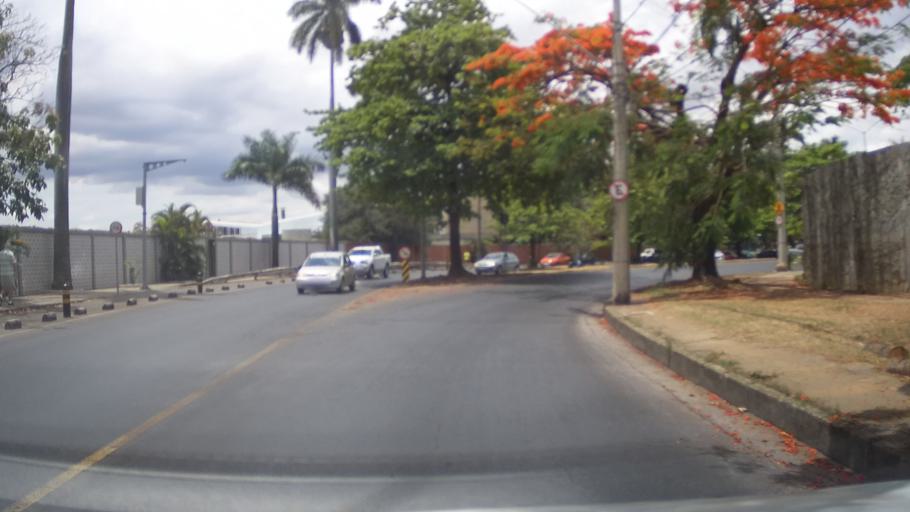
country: BR
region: Minas Gerais
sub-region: Belo Horizonte
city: Belo Horizonte
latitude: -19.8551
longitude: -43.9763
